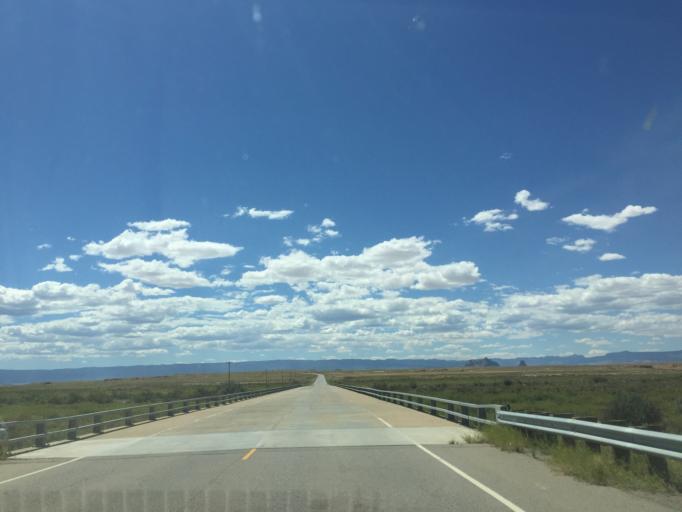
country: US
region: New Mexico
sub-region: San Juan County
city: Waterflow
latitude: 36.3683
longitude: -108.5656
